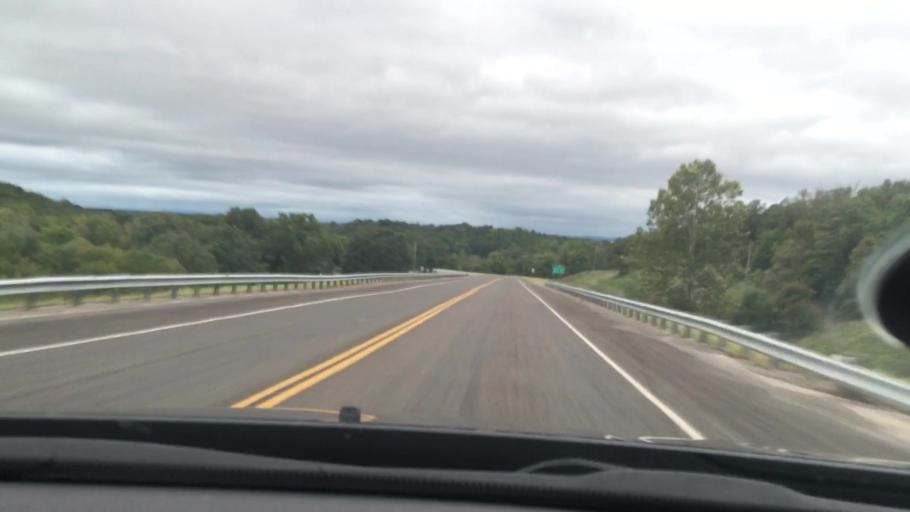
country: US
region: Oklahoma
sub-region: Sequoyah County
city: Vian
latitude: 35.5219
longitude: -94.9739
